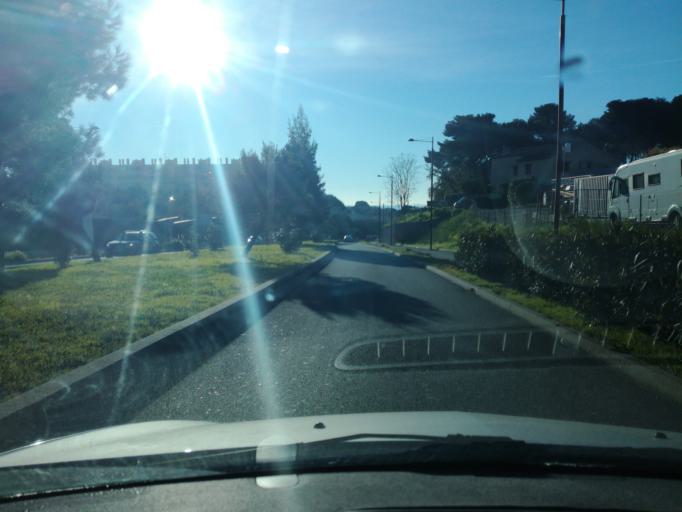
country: FR
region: Provence-Alpes-Cote d'Azur
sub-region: Departement des Alpes-Maritimes
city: Biot
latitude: 43.5951
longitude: 7.0905
